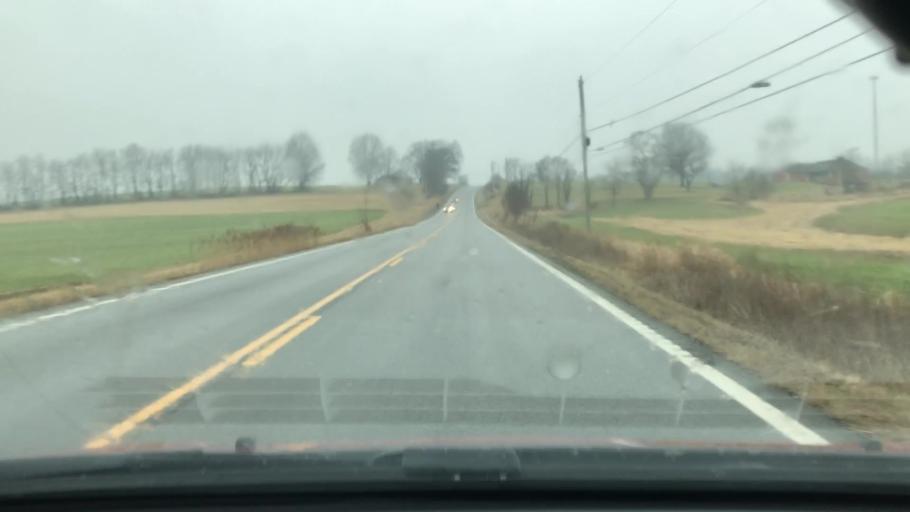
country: US
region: Ohio
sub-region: Wayne County
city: Rittman
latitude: 40.9415
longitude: -81.7465
